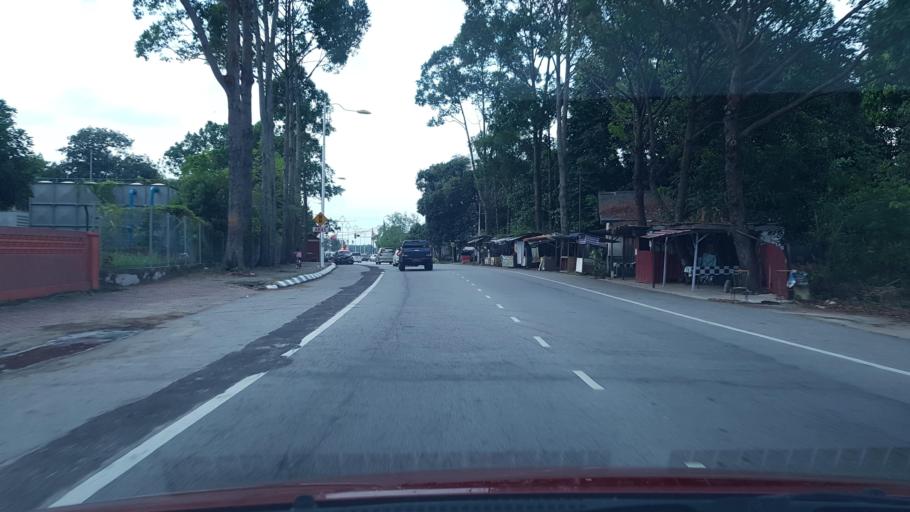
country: MY
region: Terengganu
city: Kuala Terengganu
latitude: 5.3345
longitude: 103.1424
